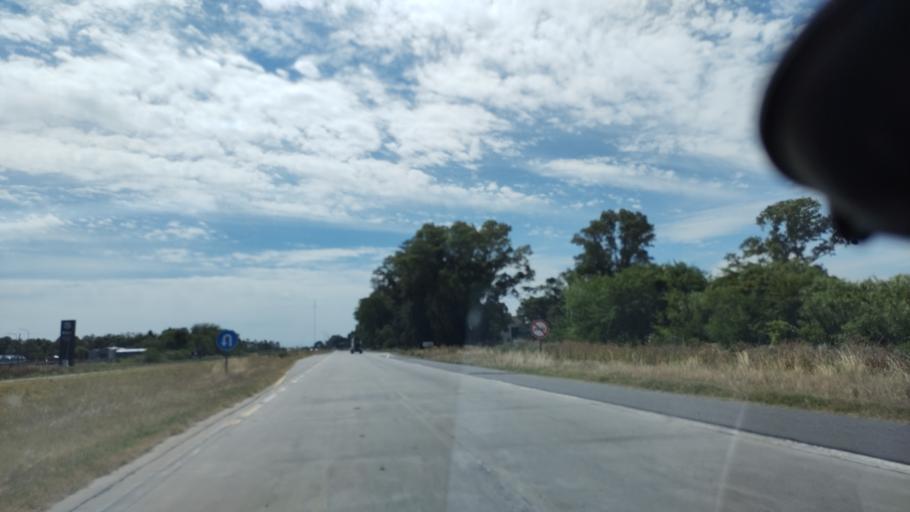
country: AR
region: Buenos Aires
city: Canuelas
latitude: -35.0382
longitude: -58.7160
